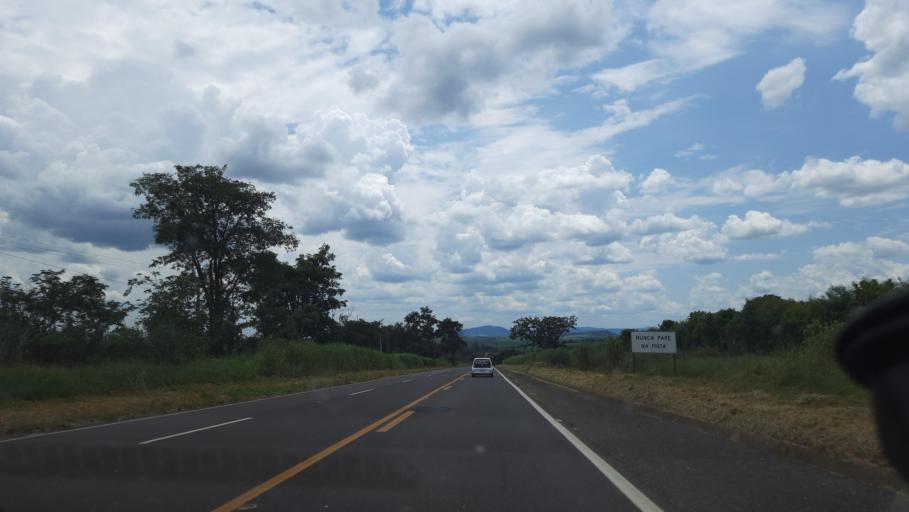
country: BR
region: Sao Paulo
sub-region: Mococa
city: Mococa
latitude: -21.4817
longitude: -47.0845
